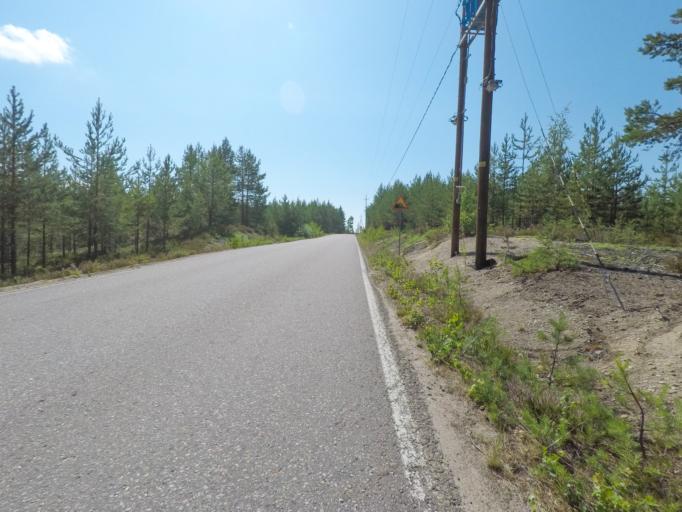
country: FI
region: Southern Savonia
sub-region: Mikkeli
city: Puumala
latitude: 61.4563
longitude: 28.1741
